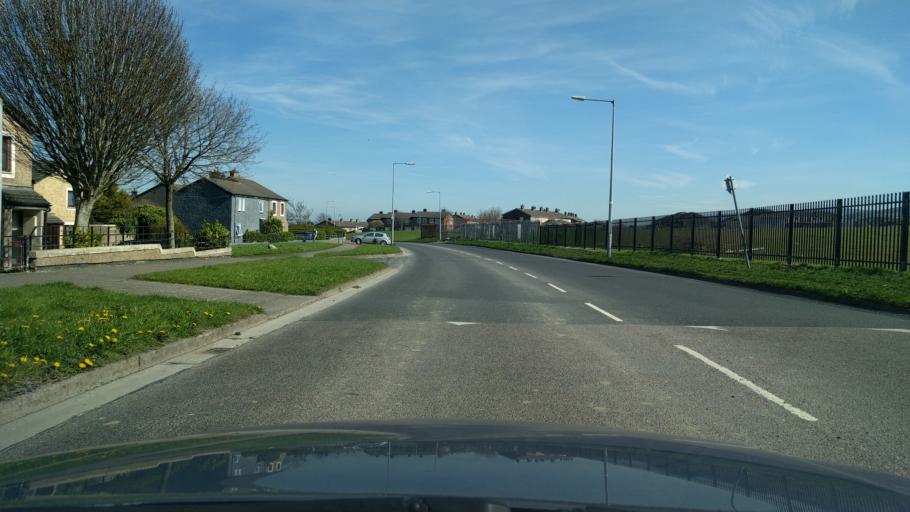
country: IE
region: Leinster
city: Oldbawn
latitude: 53.2729
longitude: -6.3836
